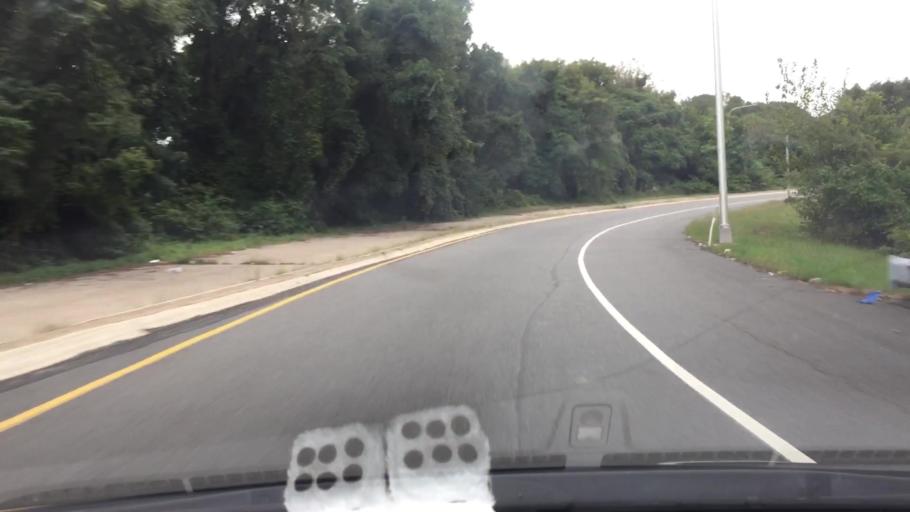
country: US
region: Pennsylvania
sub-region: Bucks County
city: Trevose
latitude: 40.1101
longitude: -74.9976
